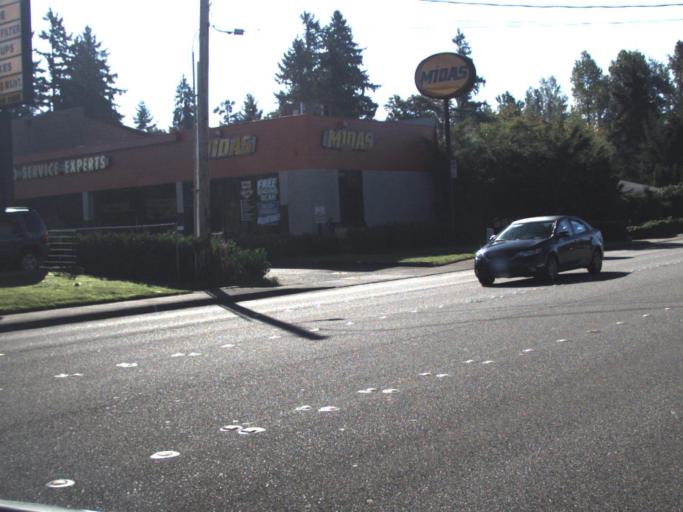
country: US
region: Washington
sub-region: King County
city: Kent
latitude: 47.3841
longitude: -122.2023
